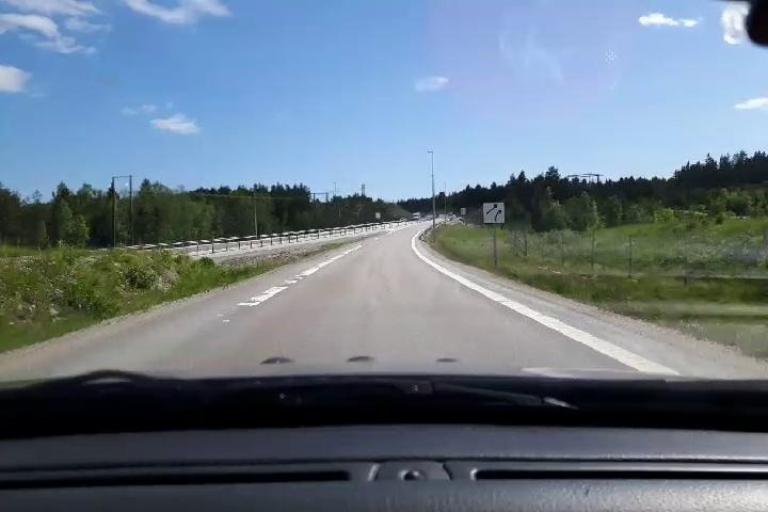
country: SE
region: Gaevleborg
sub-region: Hudiksvalls Kommun
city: Hudiksvall
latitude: 61.7130
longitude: 17.0480
